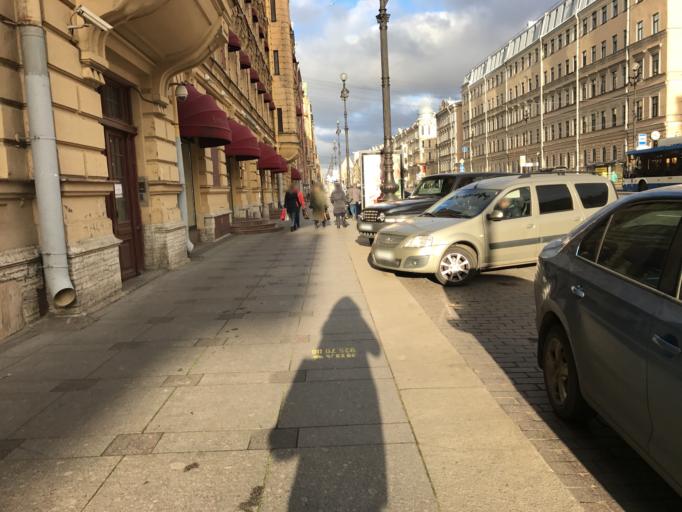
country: RU
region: St.-Petersburg
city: Centralniy
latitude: 59.9251
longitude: 30.3808
